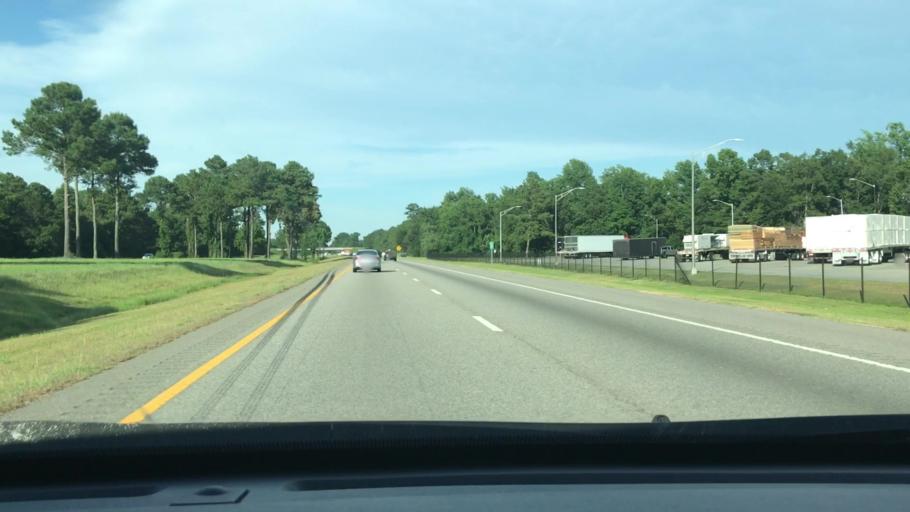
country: US
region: North Carolina
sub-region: Robeson County
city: Rowland
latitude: 34.5389
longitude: -79.2356
